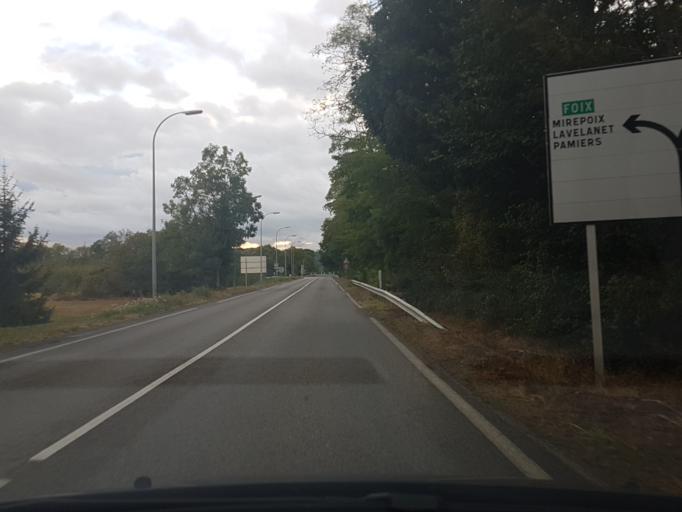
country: FR
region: Midi-Pyrenees
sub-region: Departement de l'Ariege
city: Mirepoix
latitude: 43.0963
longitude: 1.8792
